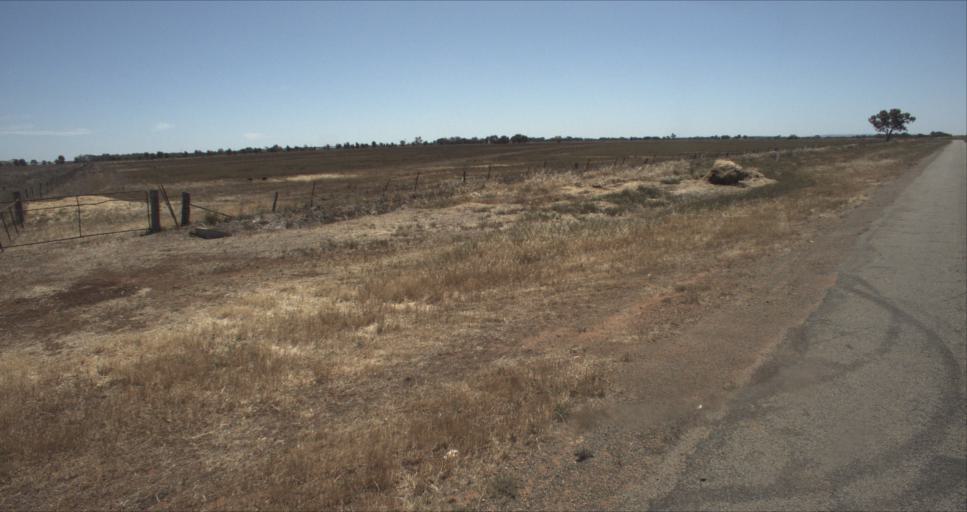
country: AU
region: New South Wales
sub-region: Leeton
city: Leeton
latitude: -34.5047
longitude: 146.3443
